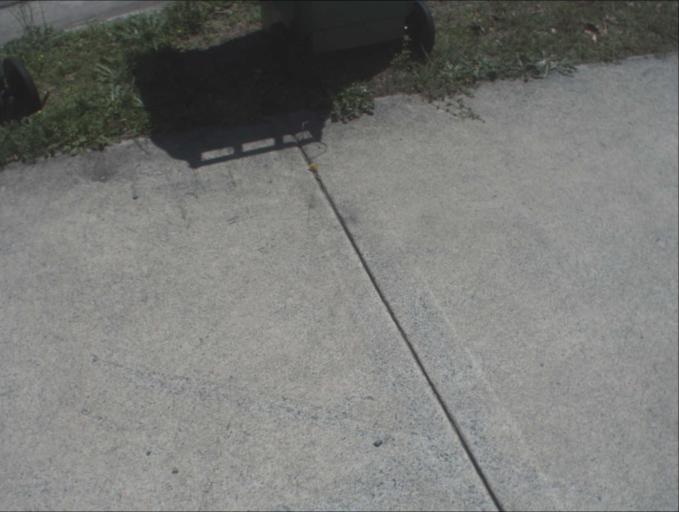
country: AU
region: Queensland
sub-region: Logan
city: Waterford West
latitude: -27.7191
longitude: 153.1545
